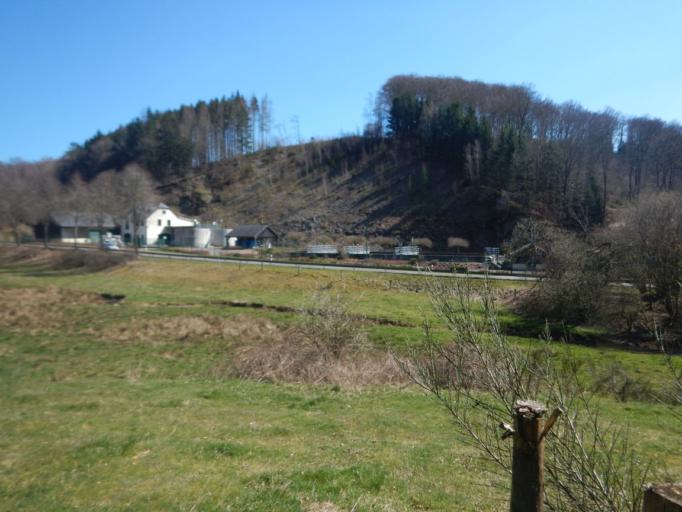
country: LU
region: Diekirch
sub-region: Canton de Clervaux
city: Weiswampach
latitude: 50.1151
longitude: 6.0475
